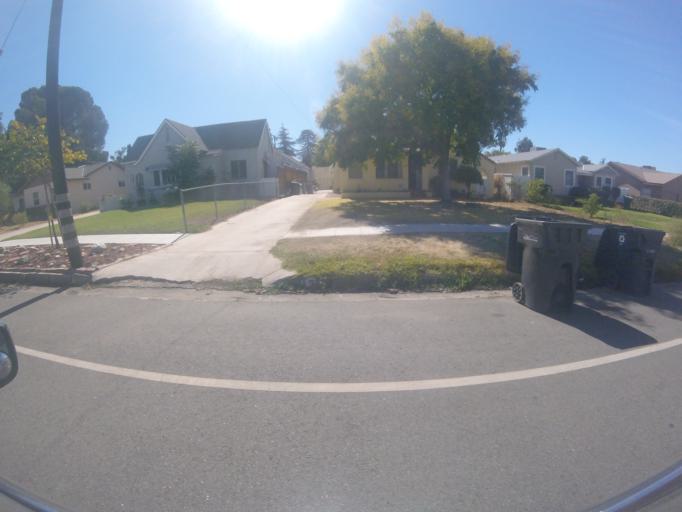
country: US
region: California
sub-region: San Bernardino County
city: Redlands
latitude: 34.0664
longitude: -117.1683
